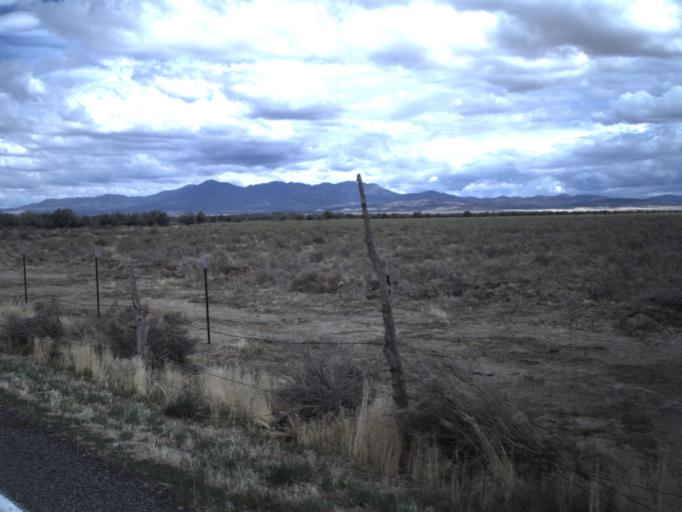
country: US
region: Utah
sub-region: Millard County
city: Fillmore
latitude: 39.0820
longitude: -112.4099
